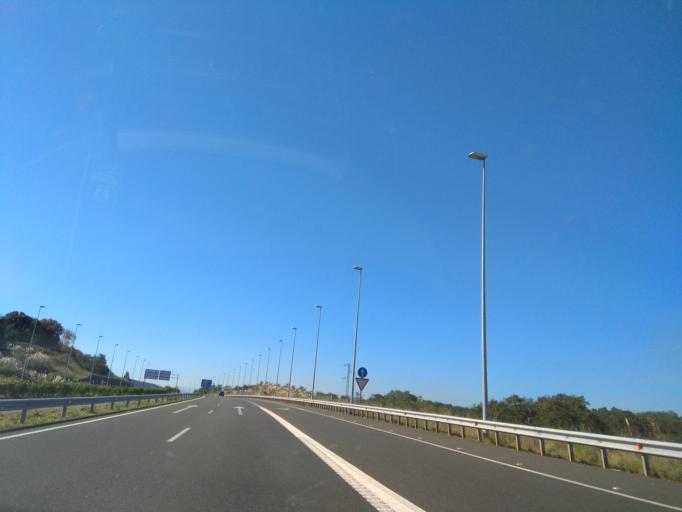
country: ES
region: Cantabria
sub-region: Provincia de Cantabria
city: El Astillero
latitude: 43.3902
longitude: -3.8348
